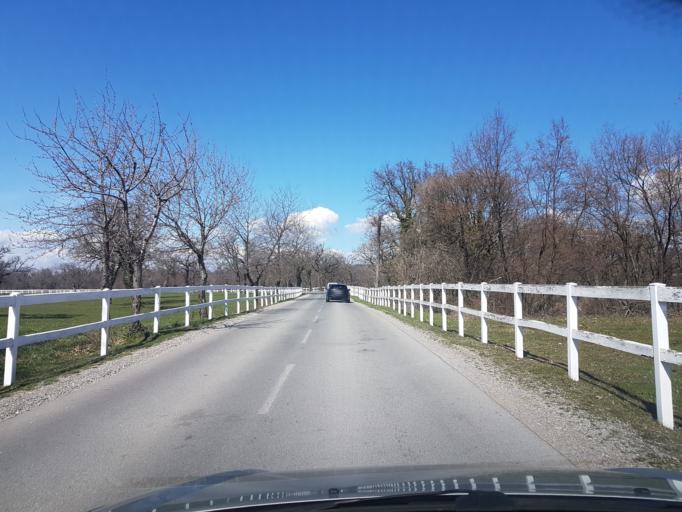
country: SI
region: Sezana
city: Sezana
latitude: 45.6685
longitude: 13.8878
